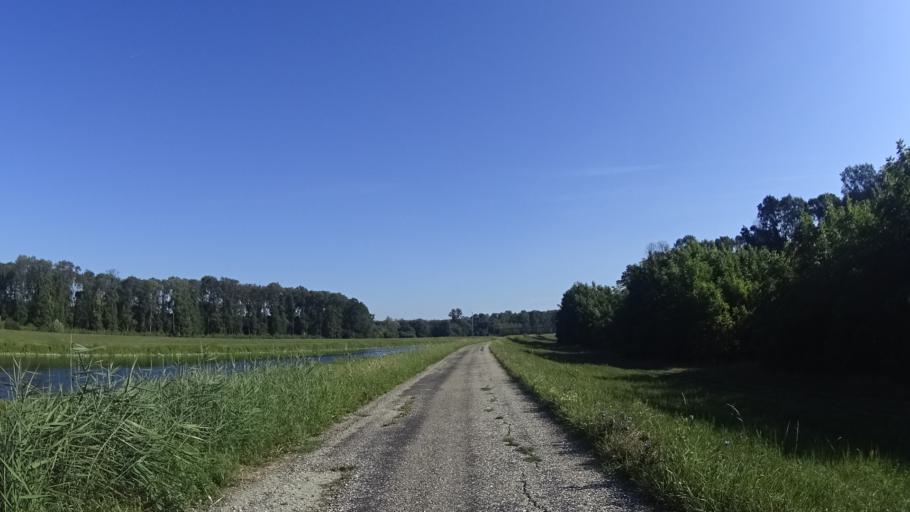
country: CZ
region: South Moravian
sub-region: Okres Breclav
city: Lanzhot
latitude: 48.7067
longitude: 16.9977
